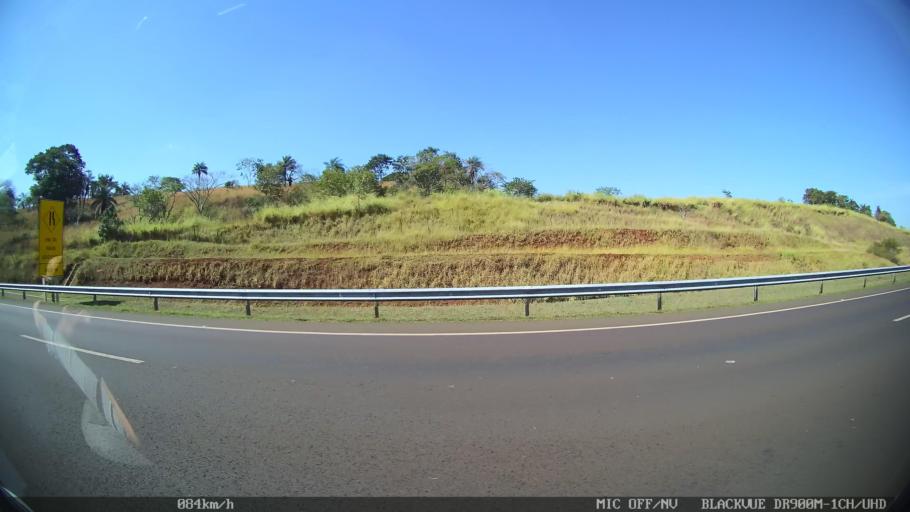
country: BR
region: Sao Paulo
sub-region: Franca
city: Franca
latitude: -20.6087
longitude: -47.4537
